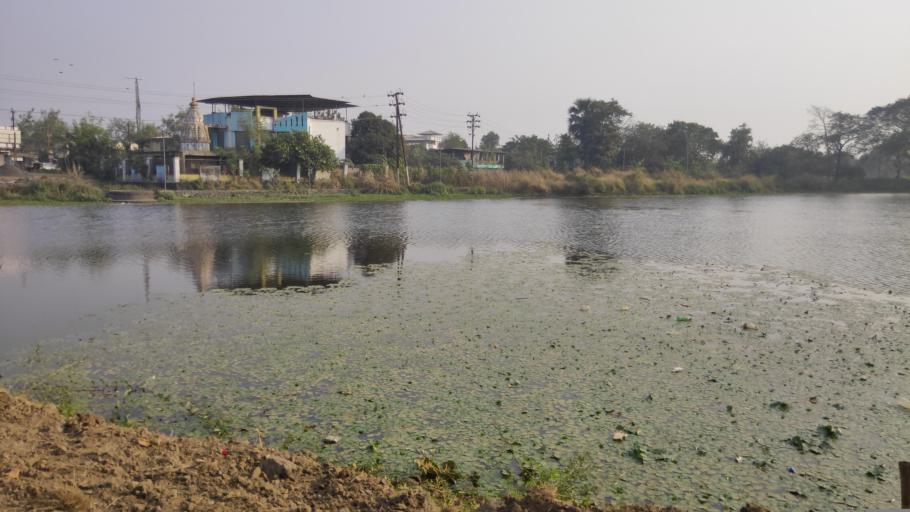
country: IN
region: Maharashtra
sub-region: Thane
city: Kalyan
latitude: 19.3007
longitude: 73.1515
